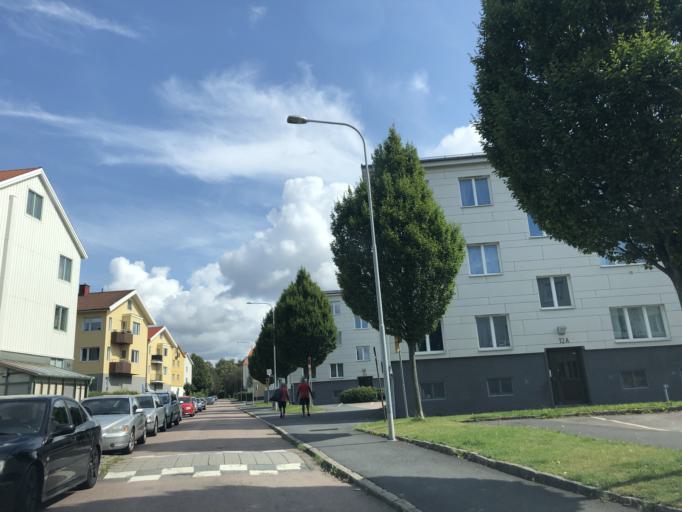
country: SE
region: Vaestra Goetaland
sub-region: Goteborg
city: Majorna
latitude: 57.7064
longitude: 11.9107
